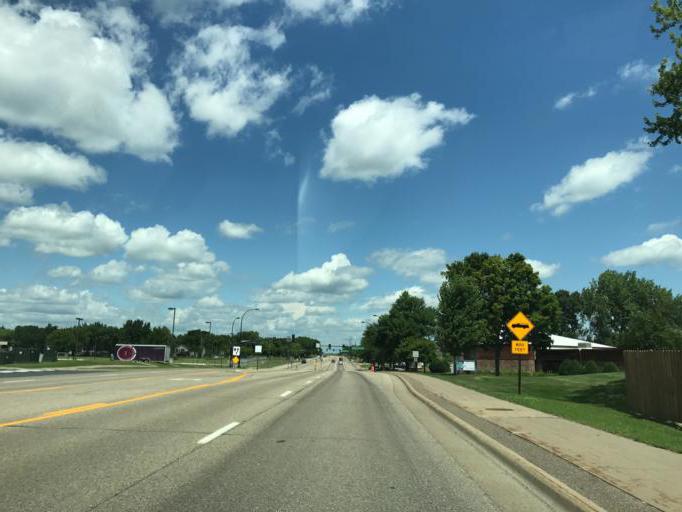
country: US
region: Minnesota
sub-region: Hennepin County
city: Maple Grove
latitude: 45.0769
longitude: -93.4311
